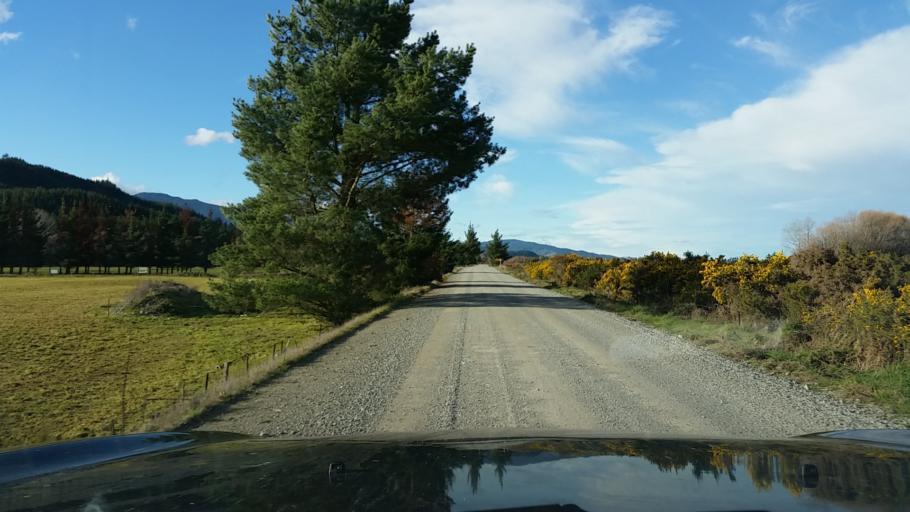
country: NZ
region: Nelson
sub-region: Nelson City
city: Nelson
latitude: -41.5702
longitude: 173.4512
